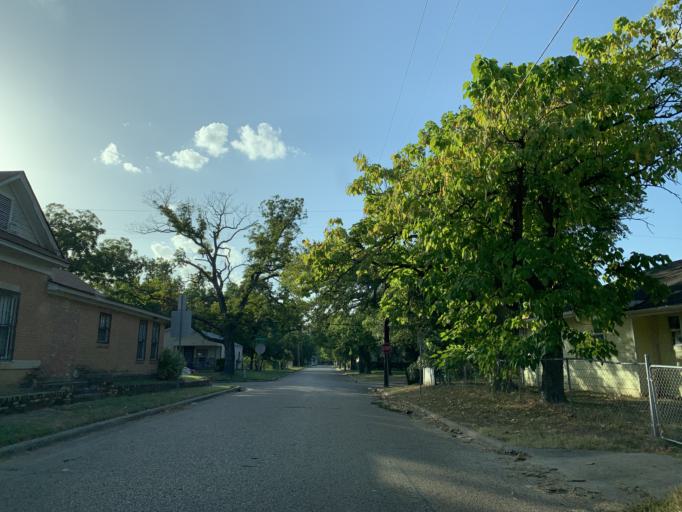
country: US
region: Texas
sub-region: Dallas County
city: Dallas
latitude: 32.7559
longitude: -96.7557
